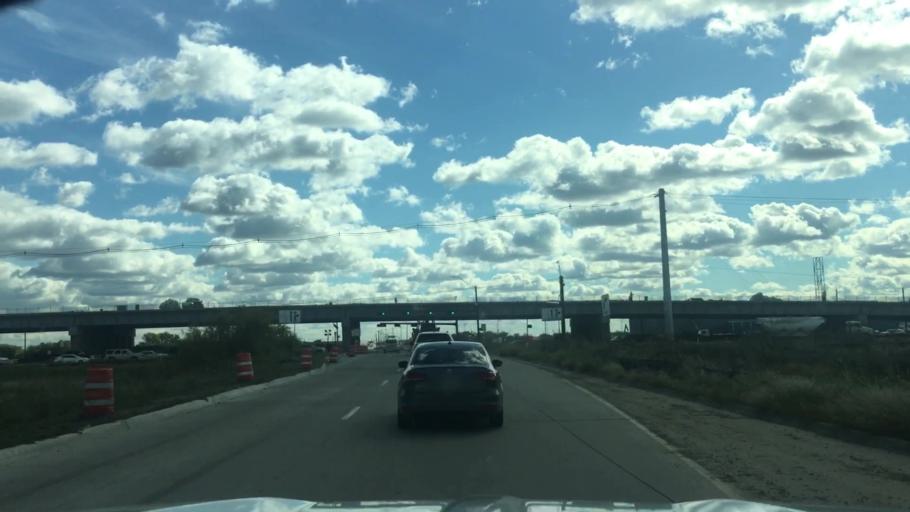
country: US
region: Texas
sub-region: Collin County
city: Prosper
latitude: 33.2203
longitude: -96.8207
